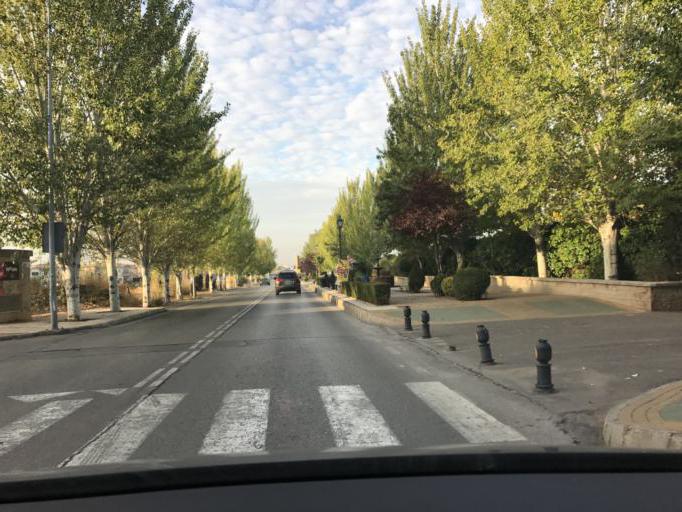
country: ES
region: Andalusia
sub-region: Provincia de Granada
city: Peligros
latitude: 37.2317
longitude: -3.6341
